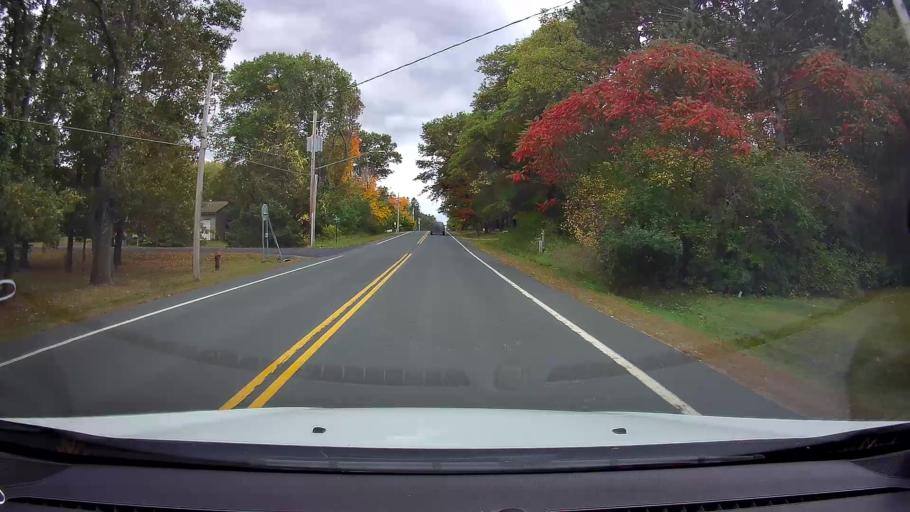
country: US
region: Wisconsin
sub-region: Polk County
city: Saint Croix Falls
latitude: 45.4175
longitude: -92.6621
